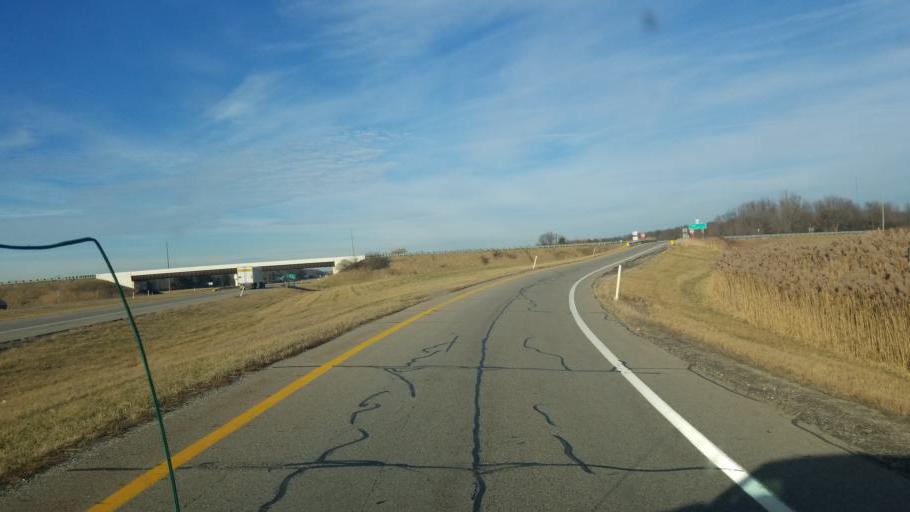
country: US
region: Ohio
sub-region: Ashtabula County
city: Orwell
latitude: 41.5337
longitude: -80.7130
